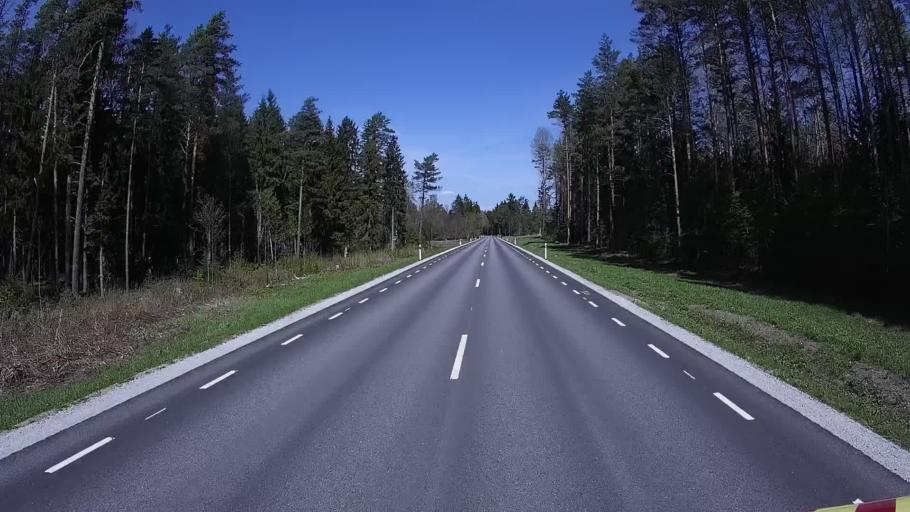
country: EE
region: Harju
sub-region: Nissi vald
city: Turba
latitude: 59.1436
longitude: 24.0768
